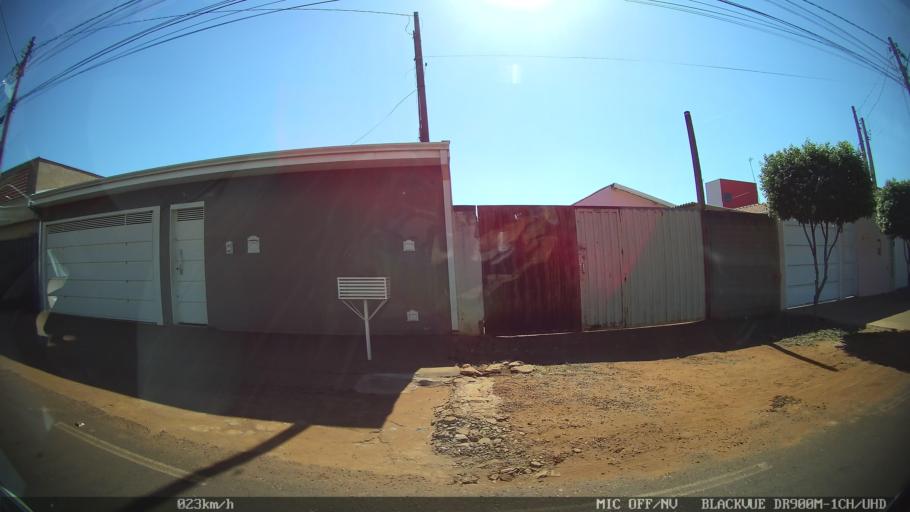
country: BR
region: Sao Paulo
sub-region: Batatais
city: Batatais
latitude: -20.8746
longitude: -47.5918
